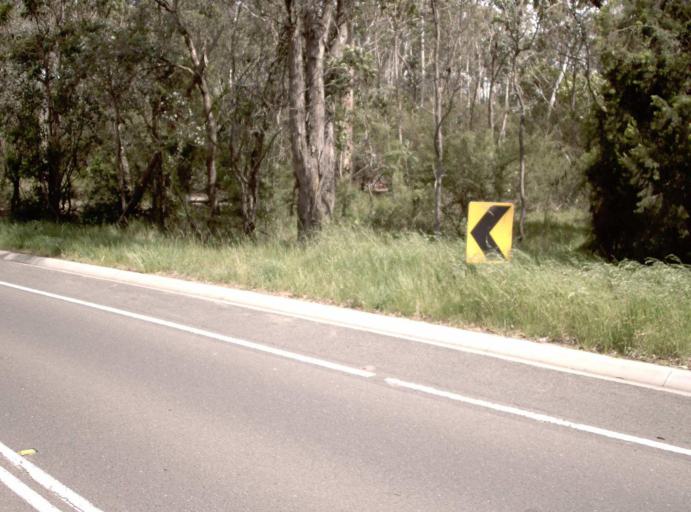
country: AU
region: Victoria
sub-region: Manningham
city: Warrandyte
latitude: -37.7577
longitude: 145.2322
